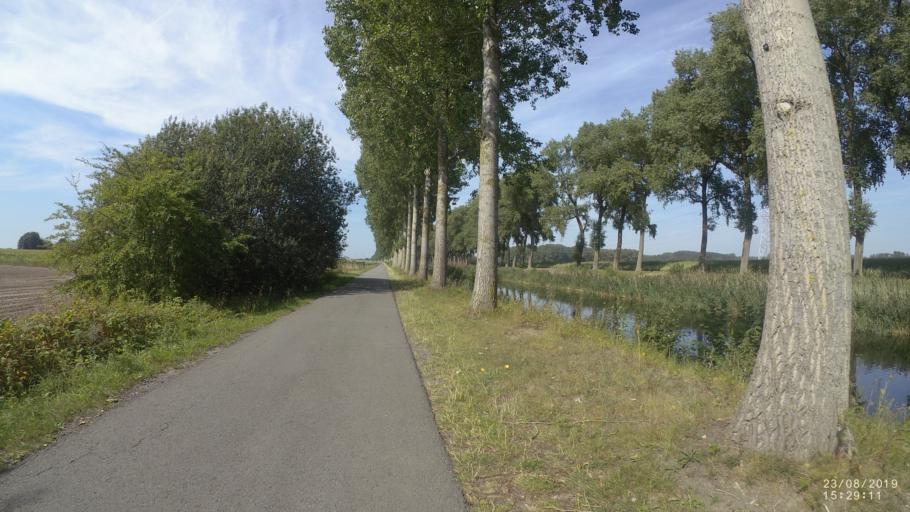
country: BE
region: Flanders
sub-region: Provincie Oost-Vlaanderen
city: Zomergem
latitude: 51.1448
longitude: 3.5554
